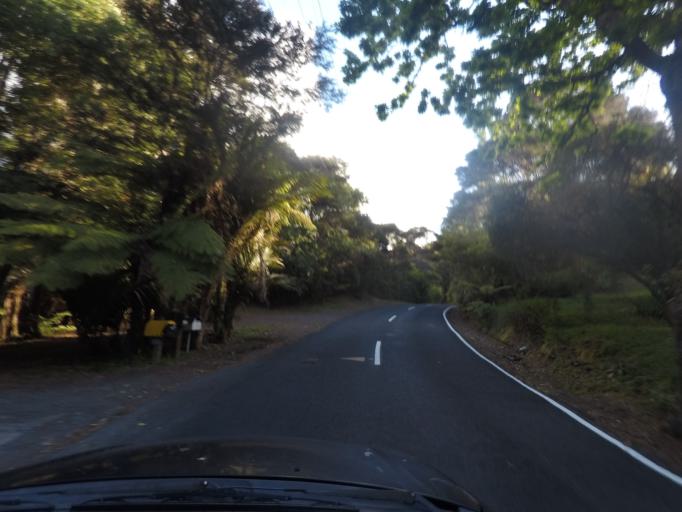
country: NZ
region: Auckland
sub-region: Auckland
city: Titirangi
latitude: -36.9339
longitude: 174.6189
